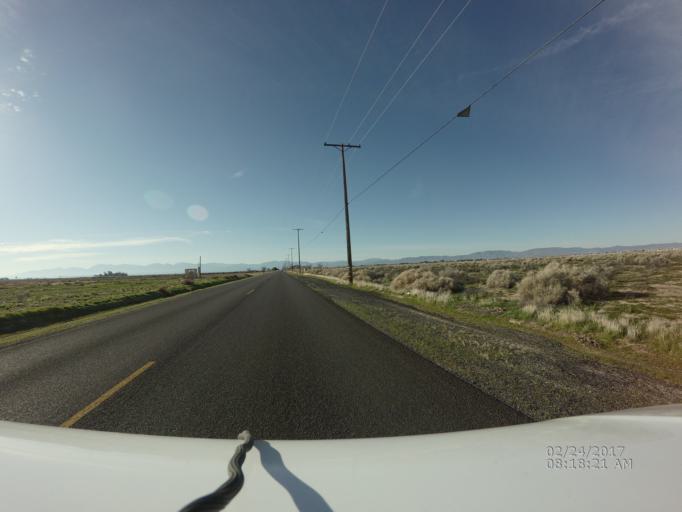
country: US
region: California
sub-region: Los Angeles County
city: Lancaster
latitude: 34.7163
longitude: -118.0412
